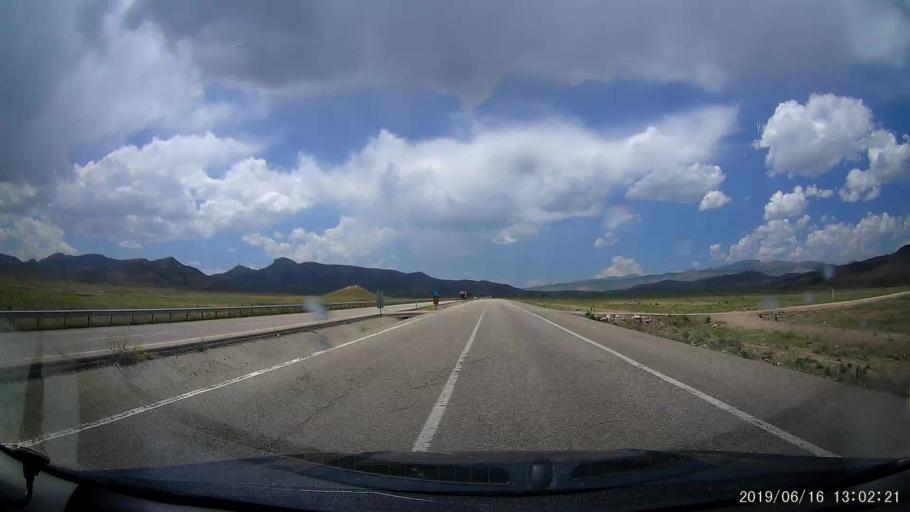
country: TR
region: Agri
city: Sulucem
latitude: 39.5741
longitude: 43.8187
